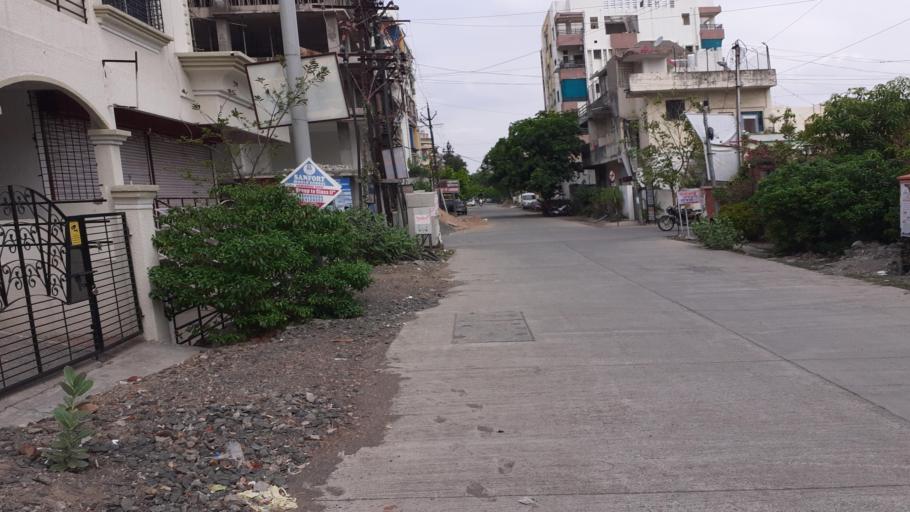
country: IN
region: Maharashtra
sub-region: Amravati Division
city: Amravati
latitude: 20.9260
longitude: 77.7649
